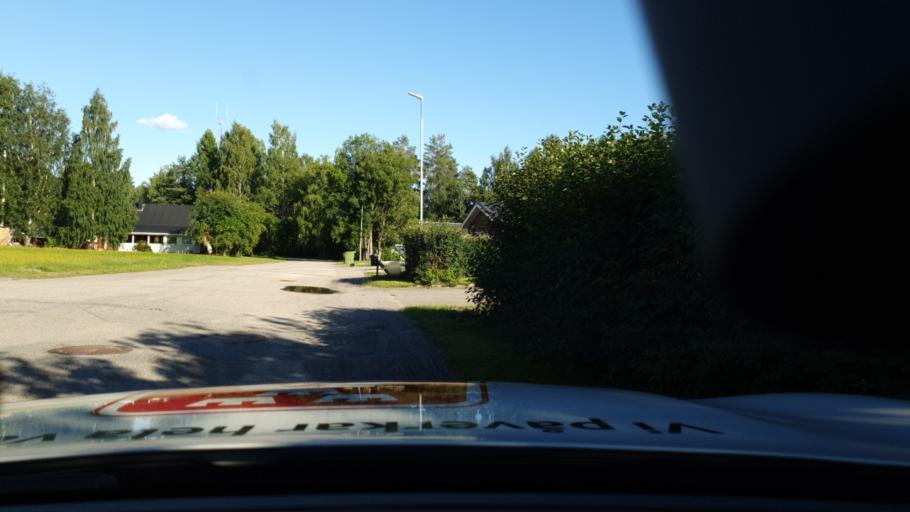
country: SE
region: Norrbotten
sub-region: Alvsbyns Kommun
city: AElvsbyn
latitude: 65.6655
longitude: 20.8617
